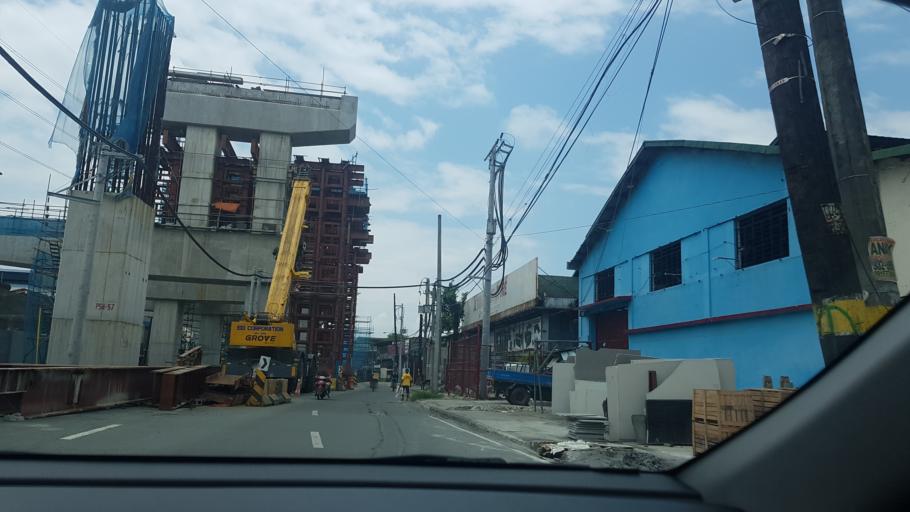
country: PH
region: Calabarzon
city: Del Monte
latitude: 14.6441
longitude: 121.0057
